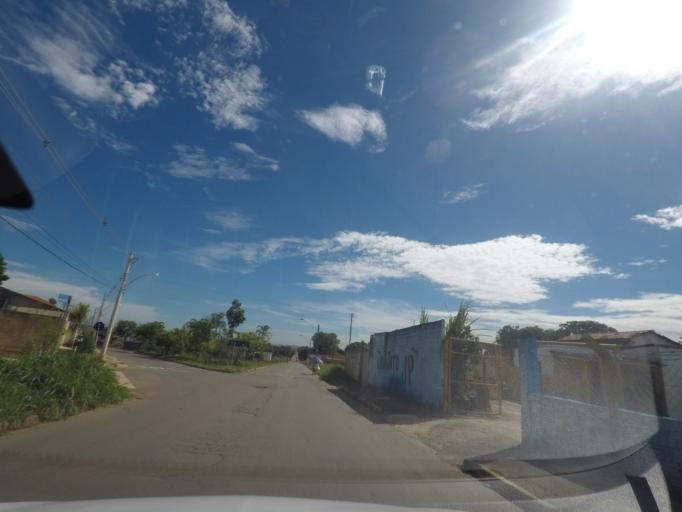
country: BR
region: Goias
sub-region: Aparecida De Goiania
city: Aparecida de Goiania
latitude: -16.8191
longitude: -49.2936
